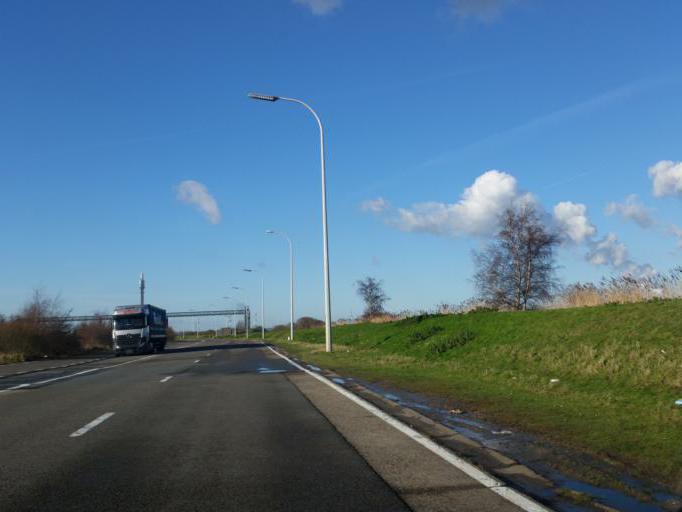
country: BE
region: Flanders
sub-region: Provincie Antwerpen
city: Zwijndrecht
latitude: 51.2472
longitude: 4.3282
